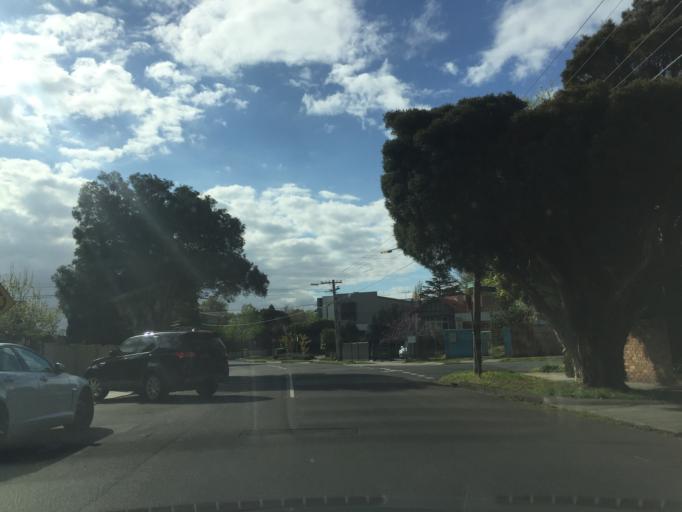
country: AU
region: Victoria
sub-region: Glen Eira
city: Caulfield North
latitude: -37.8667
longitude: 145.0164
